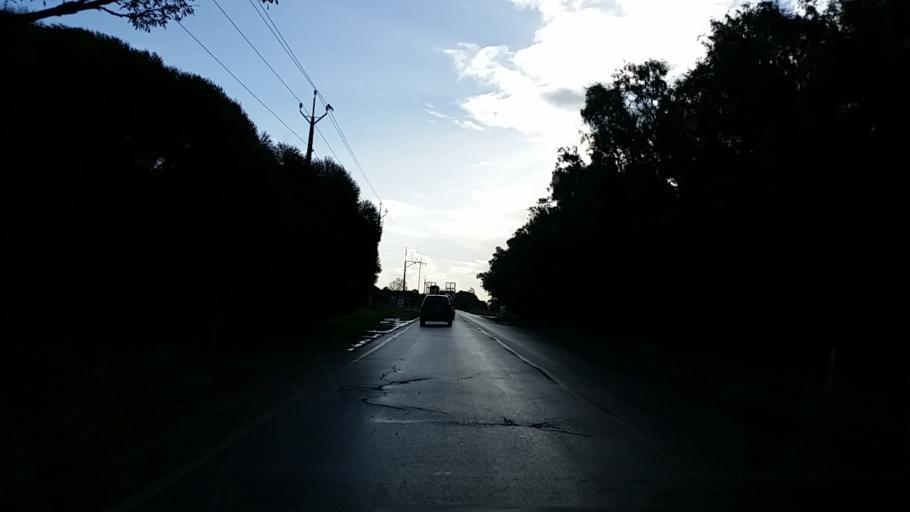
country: AU
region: South Australia
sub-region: Playford
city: Angle Vale
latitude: -34.6883
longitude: 138.6347
